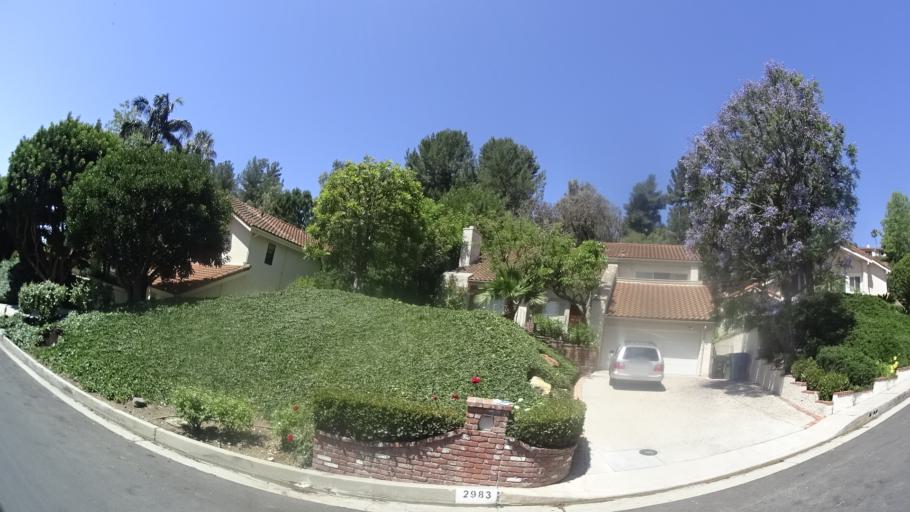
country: US
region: California
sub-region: Los Angeles County
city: Sherman Oaks
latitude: 34.1283
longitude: -118.4462
